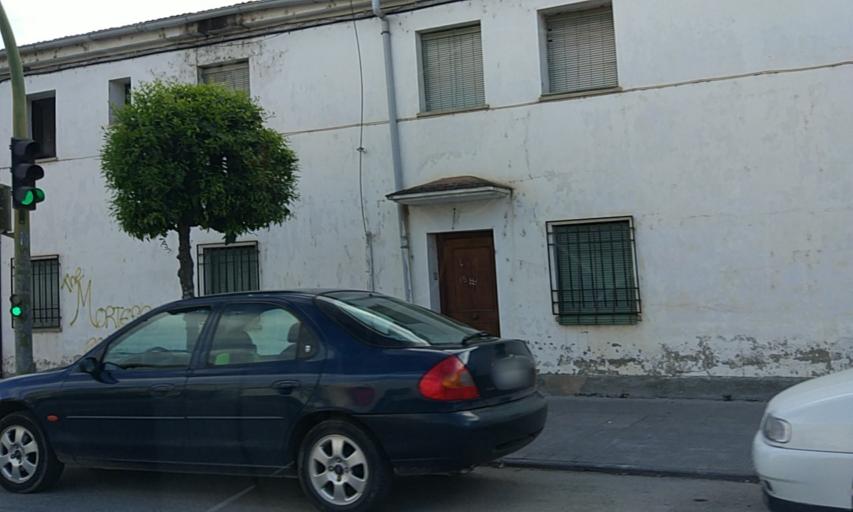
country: ES
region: Extremadura
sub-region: Provincia de Caceres
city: Moraleja
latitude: 40.0675
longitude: -6.6550
